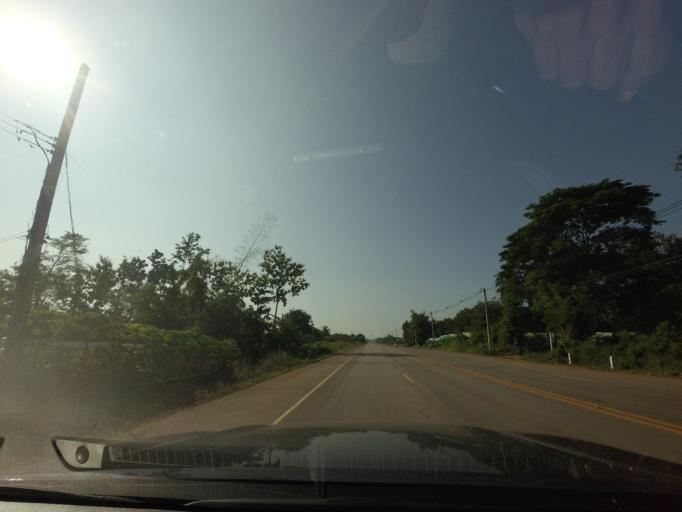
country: TH
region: Phetchabun
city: Lom Sak
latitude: 16.8228
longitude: 101.1813
